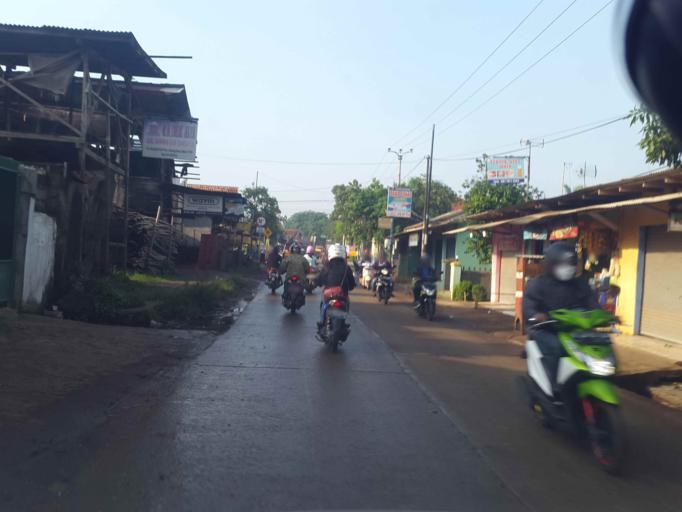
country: ID
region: West Java
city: Cileungsir
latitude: -6.3339
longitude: 107.0465
